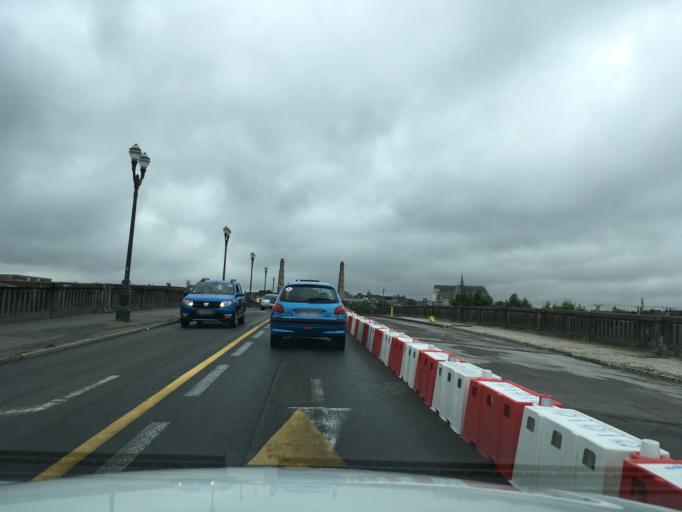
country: FR
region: Picardie
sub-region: Departement de l'Aisne
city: Harly
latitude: 49.8397
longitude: 3.2996
